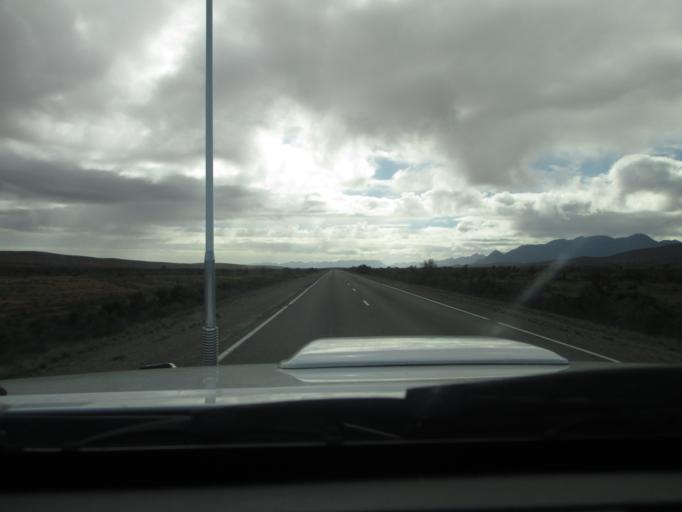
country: AU
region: South Australia
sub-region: Flinders Ranges
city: Quorn
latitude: -31.6204
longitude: 138.3936
